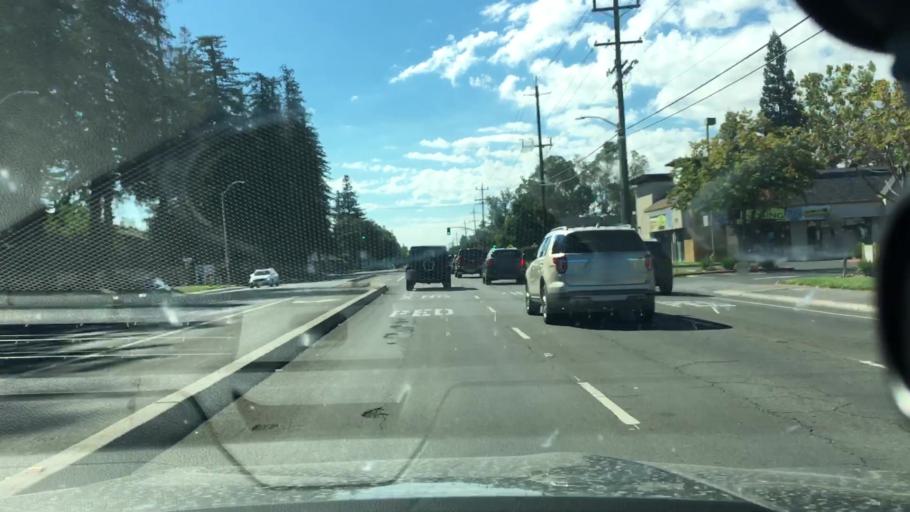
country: US
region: California
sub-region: Sacramento County
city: Arden-Arcade
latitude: 38.6271
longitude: -121.3830
